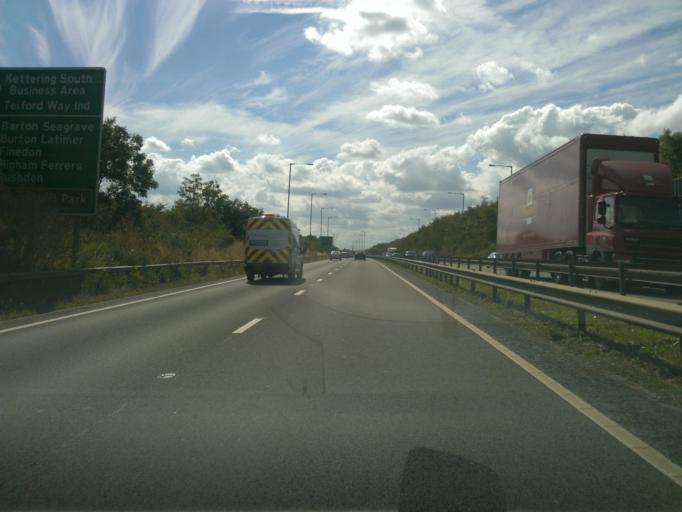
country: GB
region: England
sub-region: Northamptonshire
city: Burton Latimer
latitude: 52.3780
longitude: -0.6730
